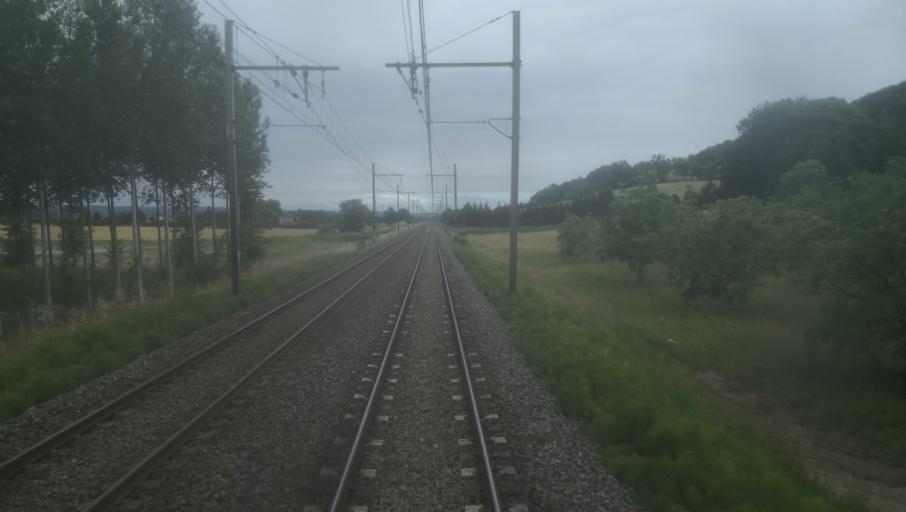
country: FR
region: Aquitaine
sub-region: Departement du Lot-et-Garonne
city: Port-Sainte-Marie
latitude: 44.2568
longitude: 0.3660
